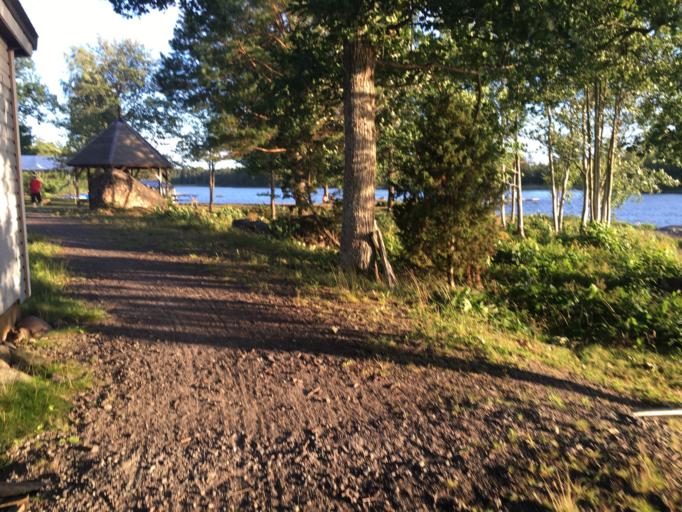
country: SE
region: Kalmar
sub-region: Nybro Kommun
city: Nybro
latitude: 56.9406
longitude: 15.9058
